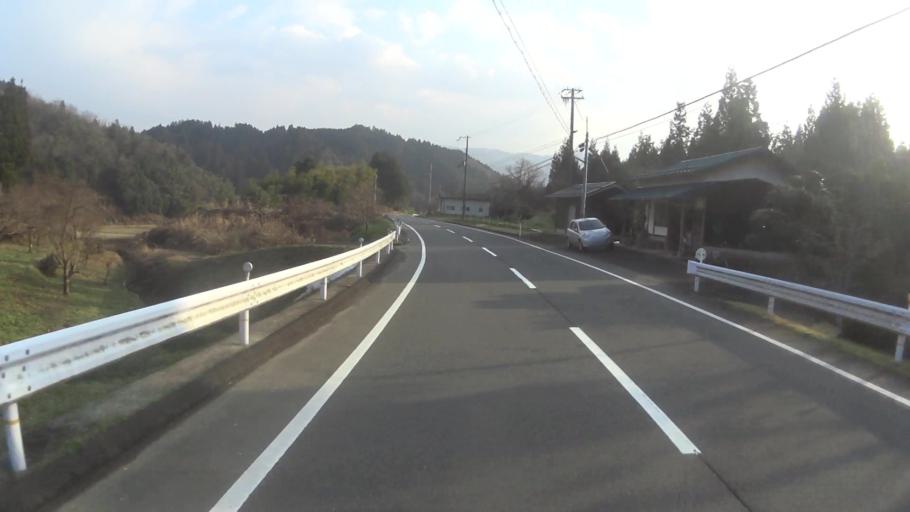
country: JP
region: Kyoto
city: Maizuru
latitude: 35.3825
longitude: 135.4180
